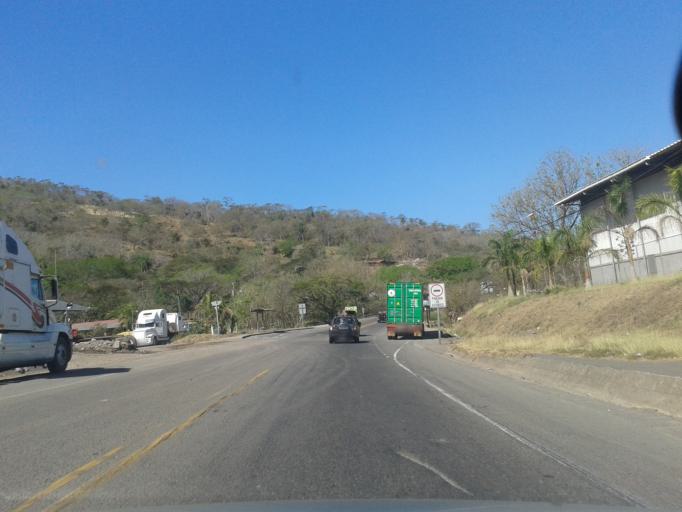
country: CR
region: Puntarenas
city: Esparza
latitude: 9.9179
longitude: -84.6996
